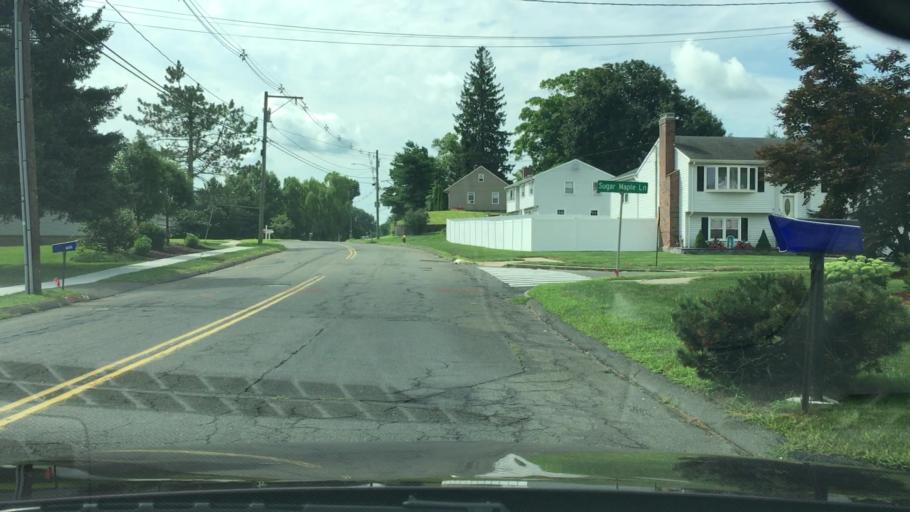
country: US
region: Connecticut
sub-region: Hartford County
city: Kensington
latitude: 41.6276
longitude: -72.7675
